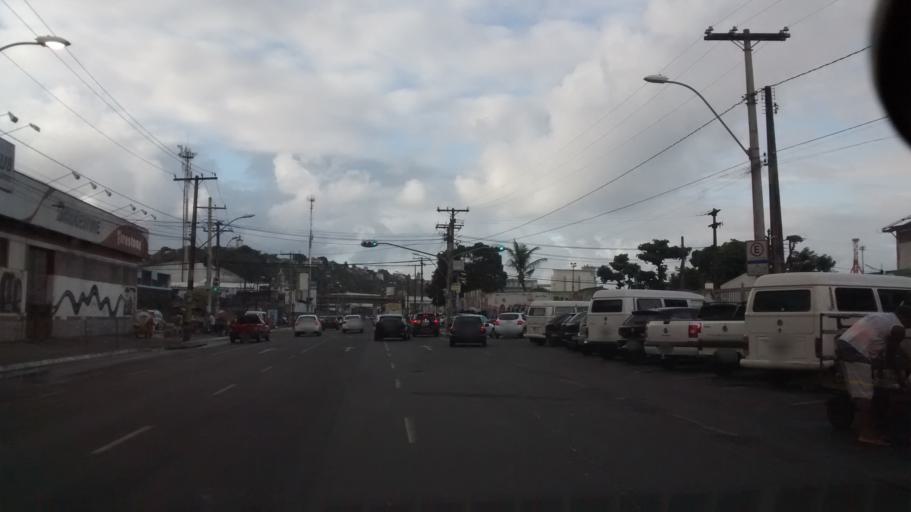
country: BR
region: Bahia
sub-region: Salvador
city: Salvador
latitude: -12.9542
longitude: -38.5020
